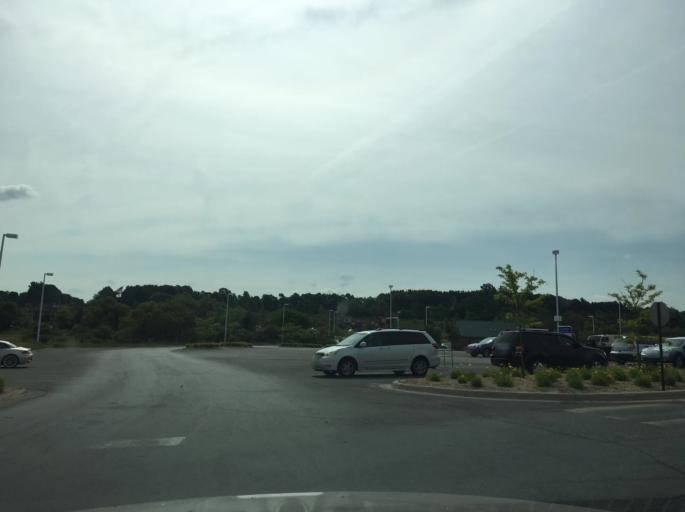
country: US
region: Michigan
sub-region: Grand Traverse County
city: Traverse City
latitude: 44.7445
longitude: -85.6440
